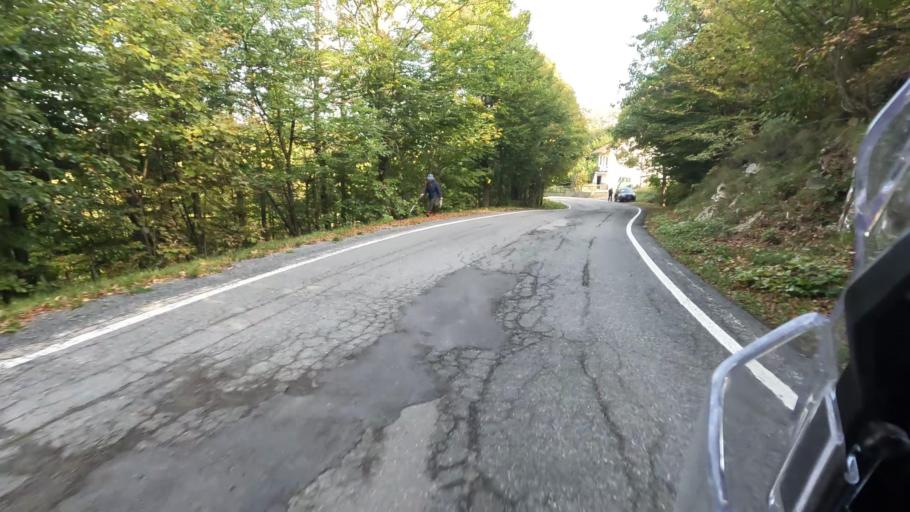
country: IT
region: Liguria
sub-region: Provincia di Savona
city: Urbe
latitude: 44.4605
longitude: 8.5522
